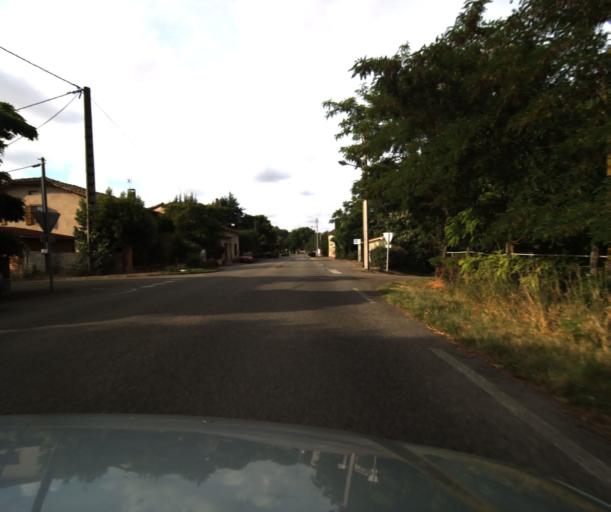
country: FR
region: Midi-Pyrenees
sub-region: Departement du Tarn-et-Garonne
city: Beaumont-de-Lomagne
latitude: 43.8509
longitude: 0.9416
